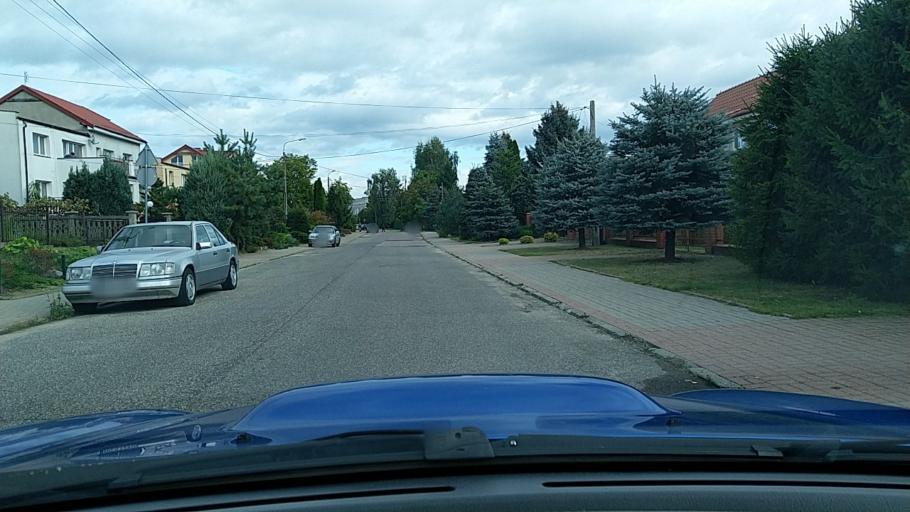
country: PL
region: Warmian-Masurian Voivodeship
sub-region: Olsztyn
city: Kortowo
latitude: 53.7659
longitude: 20.4246
